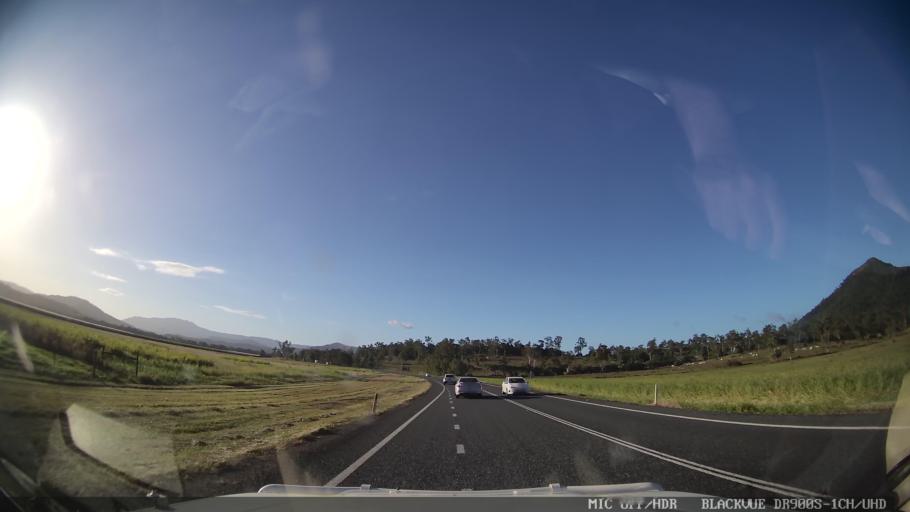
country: AU
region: Queensland
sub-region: Whitsunday
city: Proserpine
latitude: -20.3600
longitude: 148.6226
